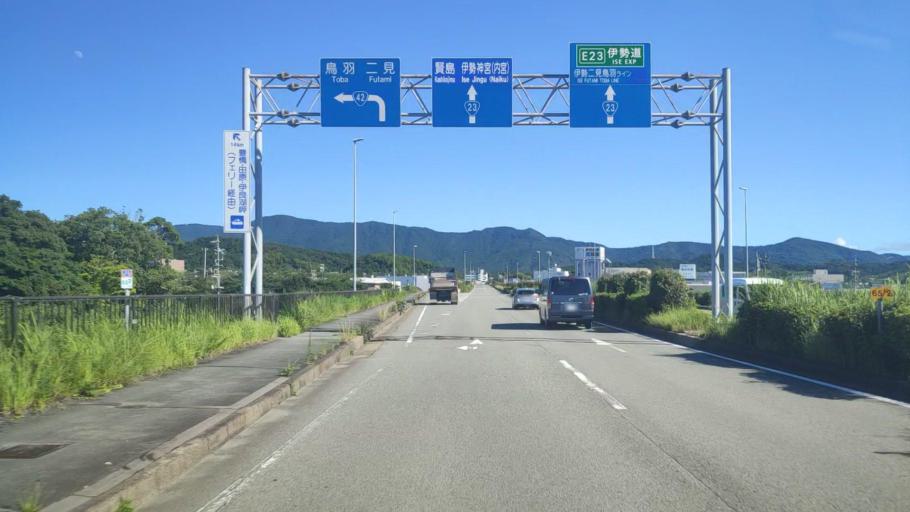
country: JP
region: Mie
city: Ise
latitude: 34.5015
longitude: 136.7387
